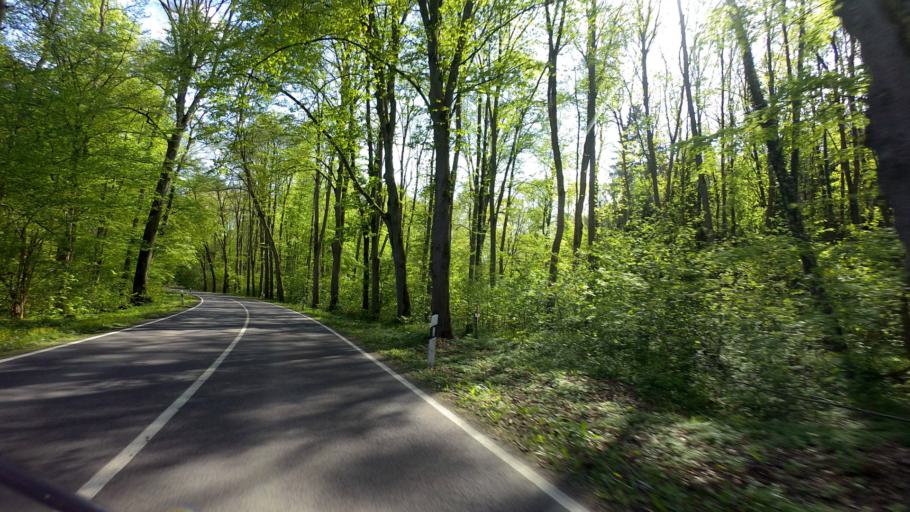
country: DE
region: Brandenburg
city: Templin
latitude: 53.0669
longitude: 13.5145
